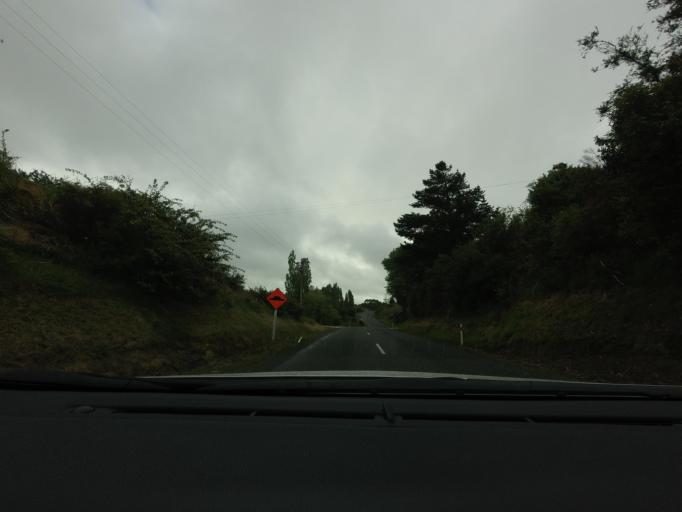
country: NZ
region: Auckland
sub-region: Auckland
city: Wellsford
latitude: -36.2930
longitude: 174.5426
